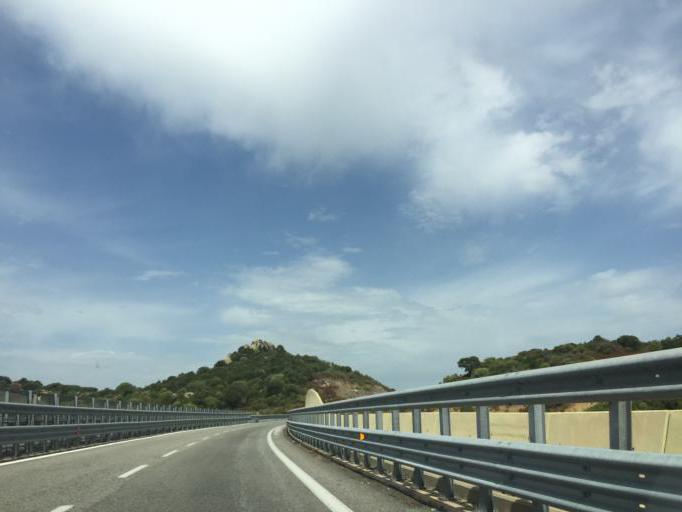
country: IT
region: Sardinia
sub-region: Provincia di Olbia-Tempio
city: San Teodoro
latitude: 40.7967
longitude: 9.5991
